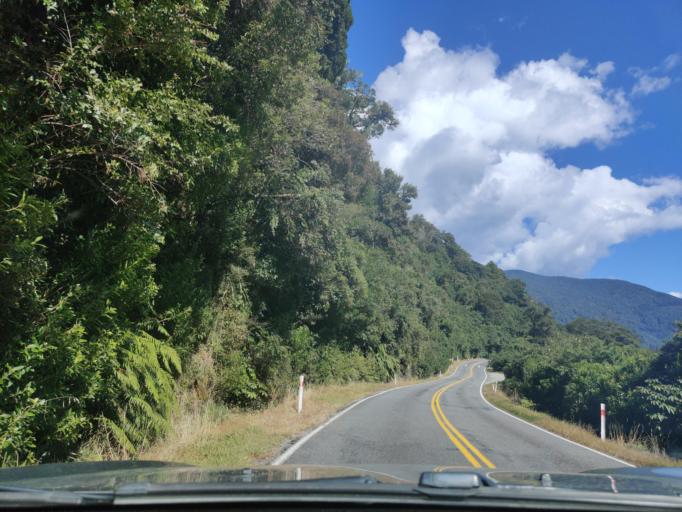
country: NZ
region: Otago
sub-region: Queenstown-Lakes District
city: Wanaka
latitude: -43.9707
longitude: 169.4125
